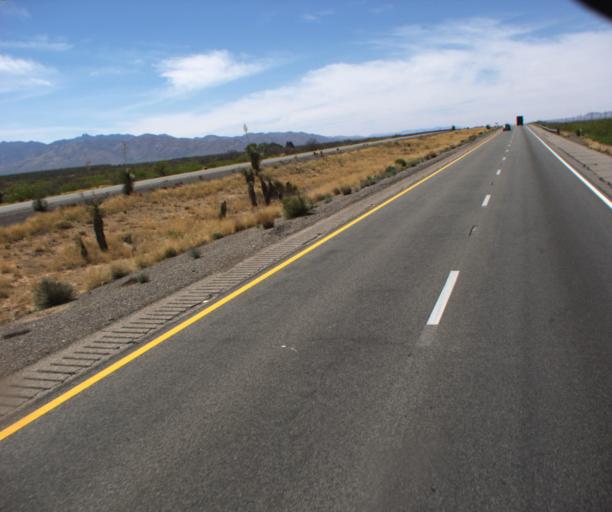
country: US
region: Arizona
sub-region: Cochise County
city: Willcox
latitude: 32.3061
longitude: -109.3918
